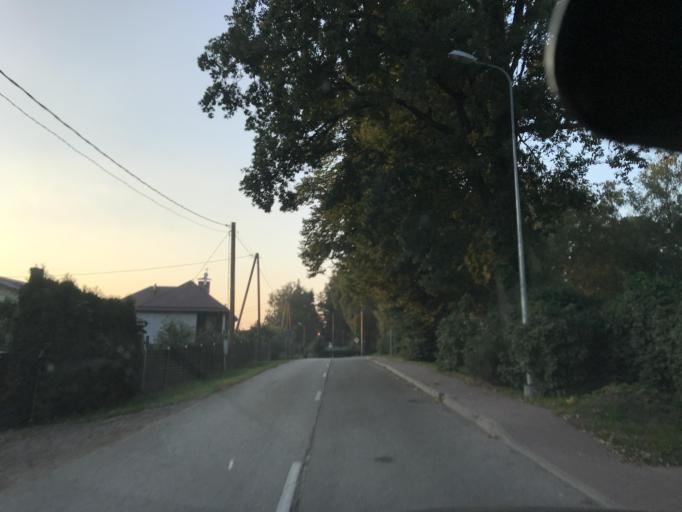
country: LV
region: Ikskile
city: Ikskile
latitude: 56.8337
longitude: 24.4921
